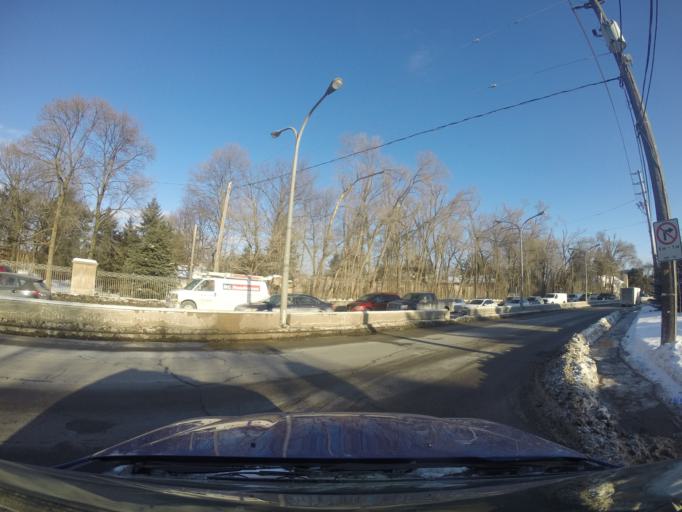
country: CA
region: Ontario
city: Toronto
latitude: 43.7256
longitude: -79.3803
